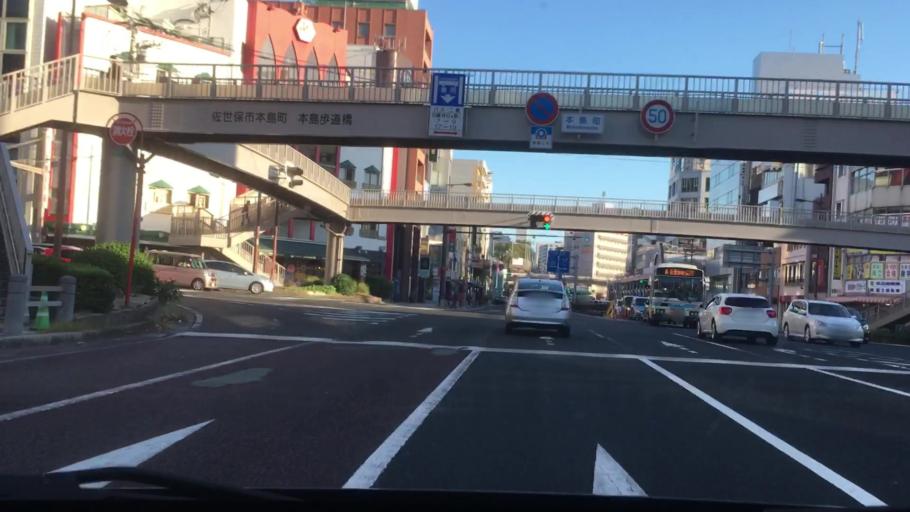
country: JP
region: Nagasaki
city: Sasebo
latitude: 33.1708
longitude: 129.7226
